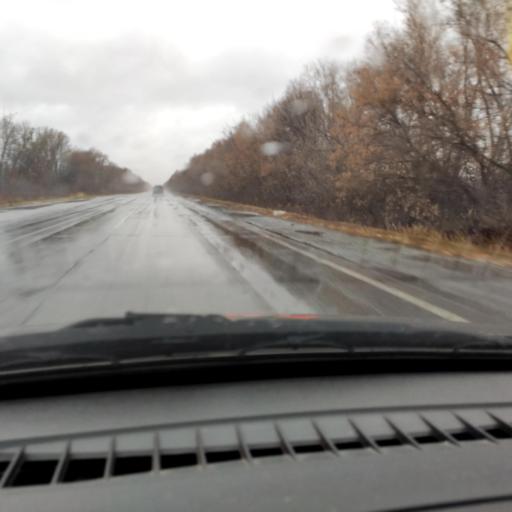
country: RU
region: Samara
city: Tol'yatti
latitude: 53.5973
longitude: 49.3249
